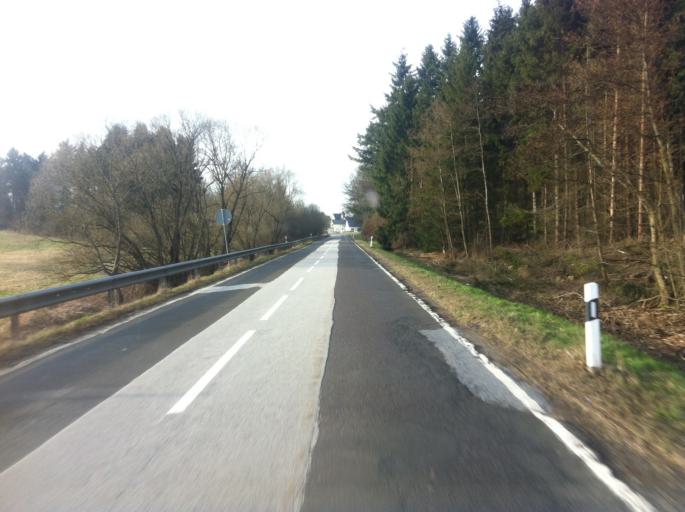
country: DE
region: Rheinland-Pfalz
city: Barenbach
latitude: 49.9420
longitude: 7.3060
